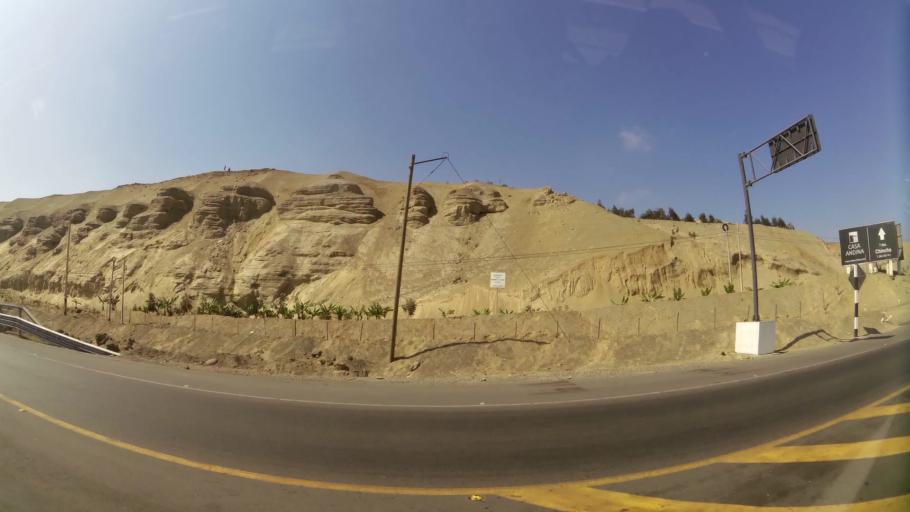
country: PE
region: Ica
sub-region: Provincia de Chincha
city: Sunampe
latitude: -13.4110
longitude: -76.1903
